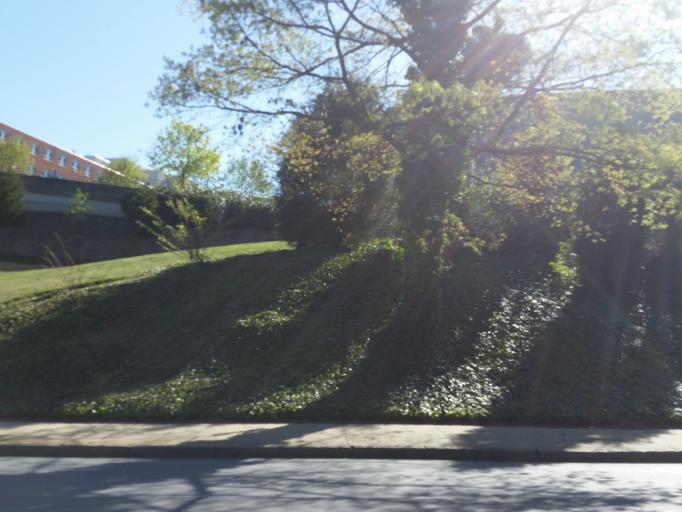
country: US
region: North Carolina
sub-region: Buncombe County
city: Asheville
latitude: 35.5778
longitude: -82.5481
